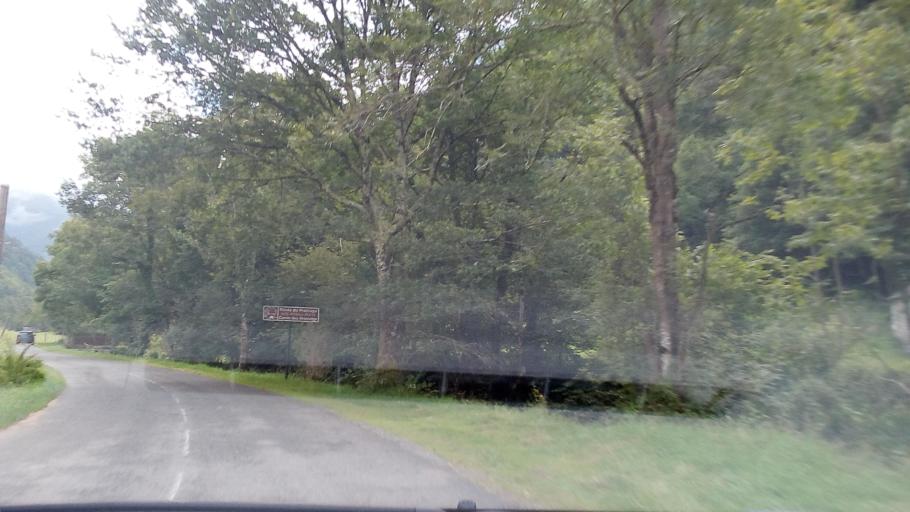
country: FR
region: Aquitaine
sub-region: Departement des Pyrenees-Atlantiques
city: Oloron-Sainte-Marie
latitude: 43.0770
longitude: -0.6000
